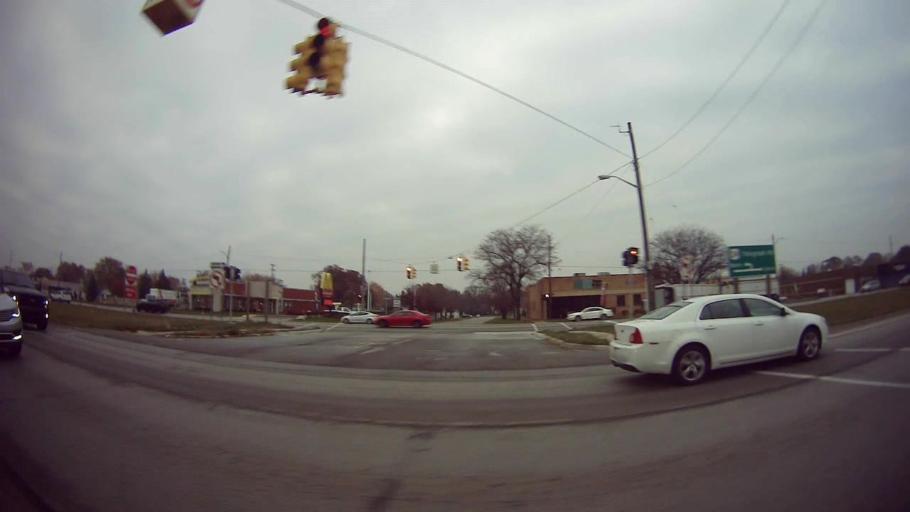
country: US
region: Michigan
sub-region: Wayne County
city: Dearborn Heights
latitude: 42.3342
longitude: -83.2732
